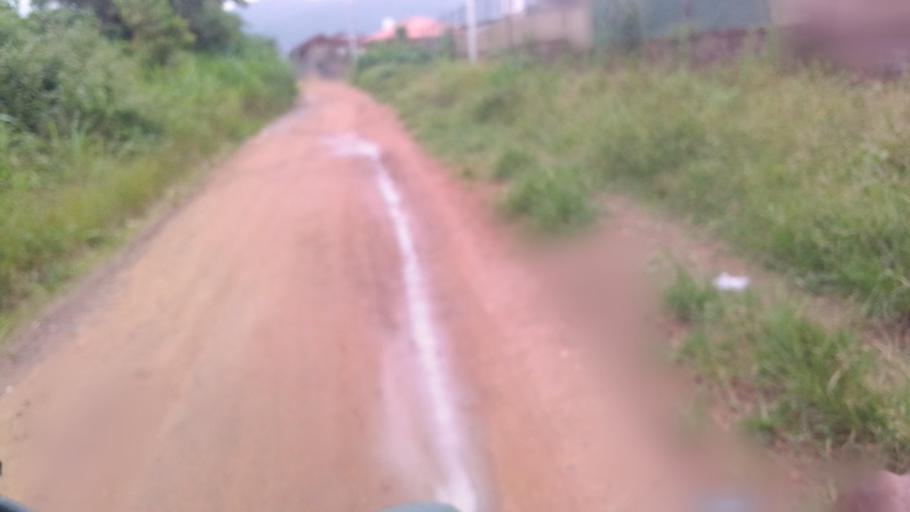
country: SL
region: Eastern Province
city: Hangha
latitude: 7.9461
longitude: -11.1413
